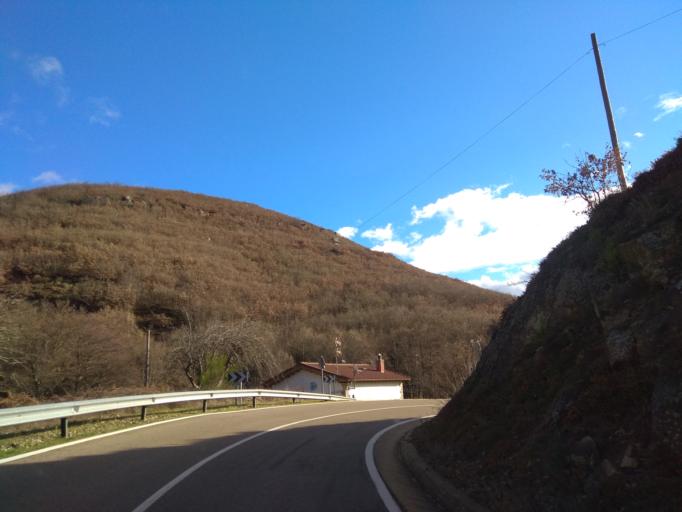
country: ES
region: Cantabria
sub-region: Provincia de Cantabria
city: San Martin de Elines
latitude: 42.8591
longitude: -3.9129
